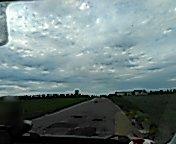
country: RU
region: Penza
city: Lermontovo
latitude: 52.9966
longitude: 43.6728
